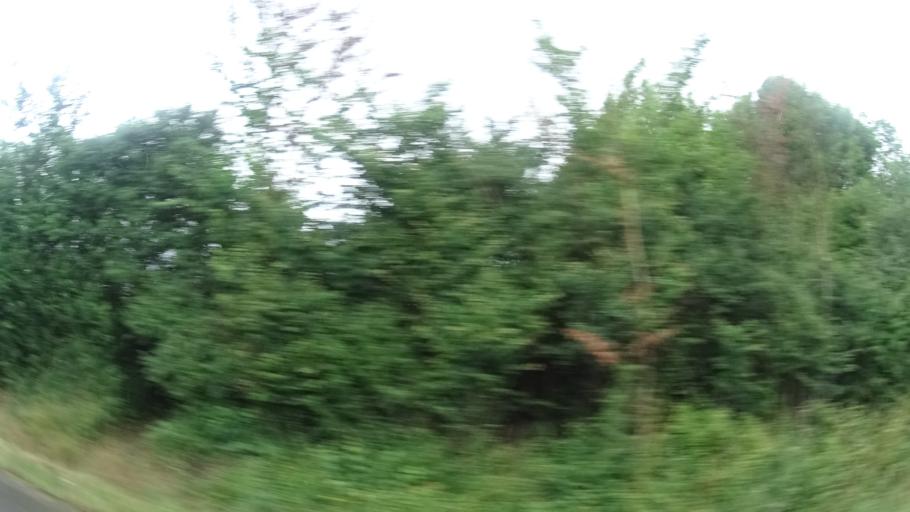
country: LU
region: Luxembourg
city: Aspelt
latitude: 49.5199
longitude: 6.2194
